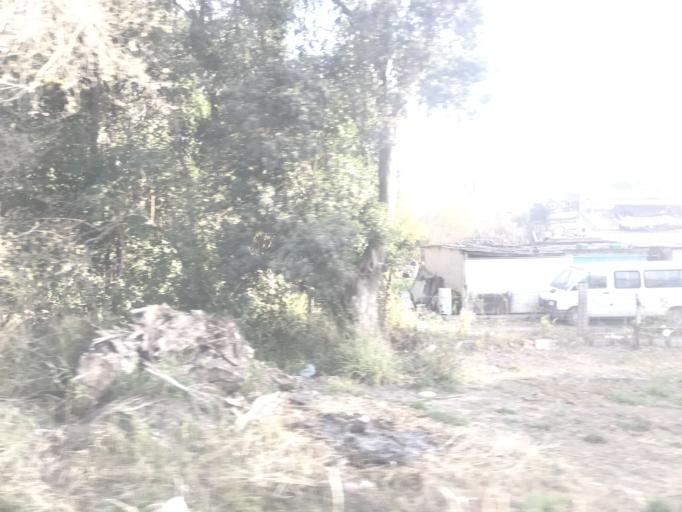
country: AR
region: Cordoba
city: Malvinas Argentinas
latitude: -31.4638
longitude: -64.1044
